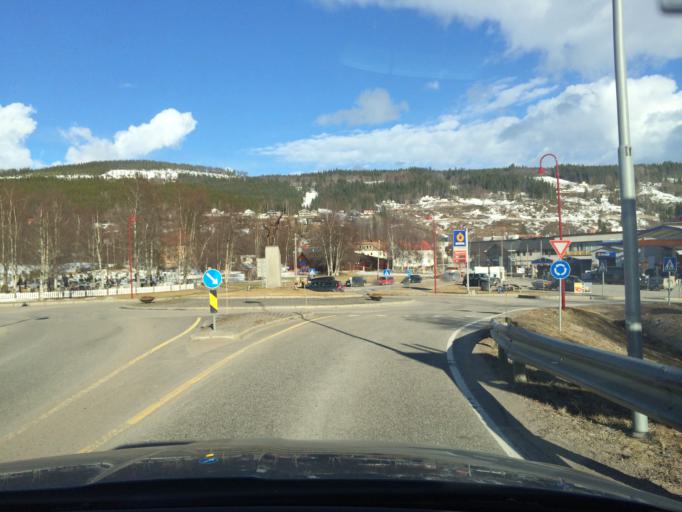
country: NO
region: Hedmark
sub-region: Trysil
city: Innbygda
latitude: 61.3162
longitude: 12.2594
